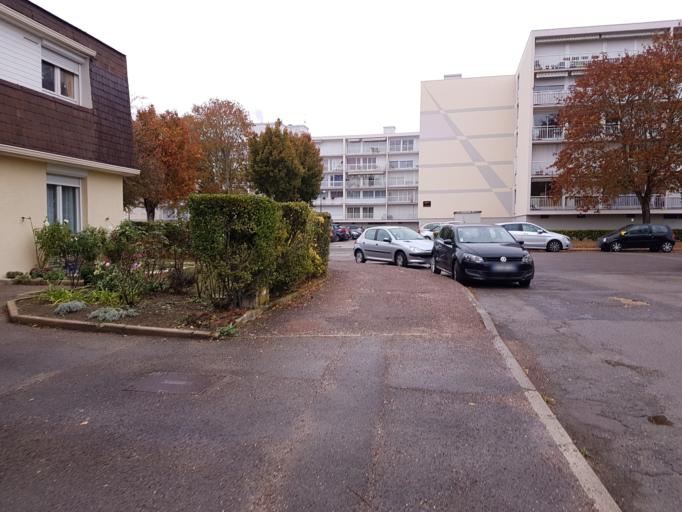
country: FR
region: Bourgogne
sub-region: Departement de la Cote-d'Or
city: Chevigny-Saint-Sauveur
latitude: 47.2982
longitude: 5.1380
